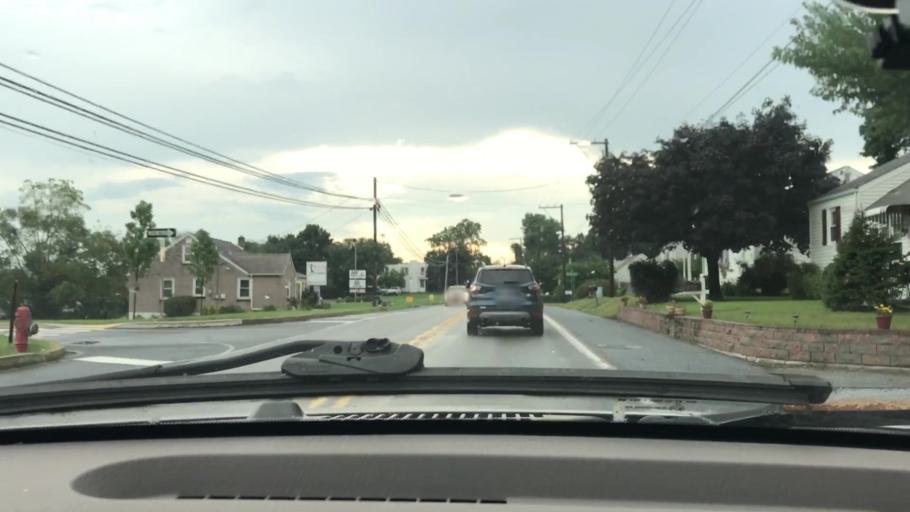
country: US
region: Pennsylvania
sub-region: Dauphin County
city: Colonial Park
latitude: 40.2930
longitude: -76.7972
